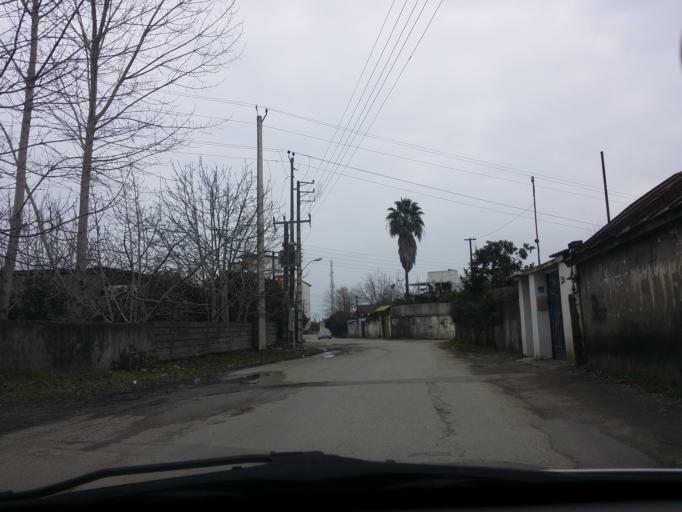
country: IR
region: Mazandaran
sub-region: Nowshahr
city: Nowshahr
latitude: 36.6539
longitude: 51.4764
